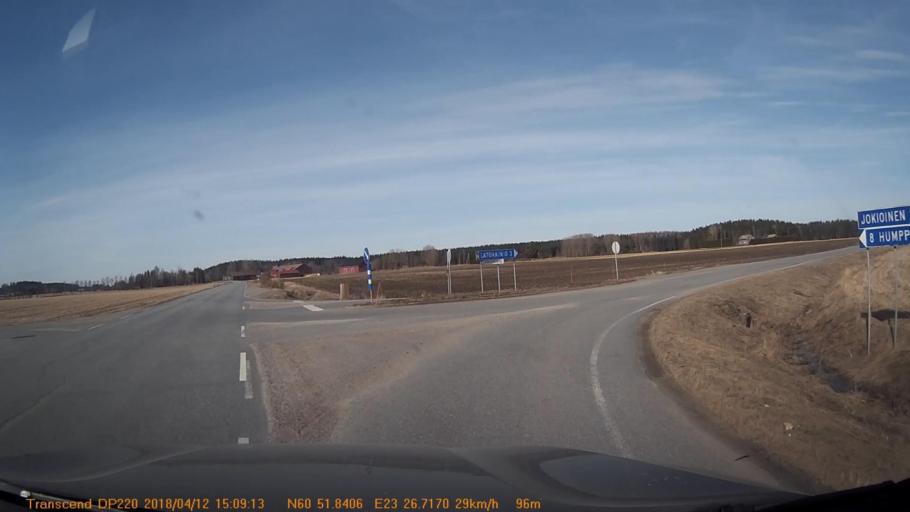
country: FI
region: Haeme
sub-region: Forssa
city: Jokioinen
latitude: 60.8637
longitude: 23.4456
